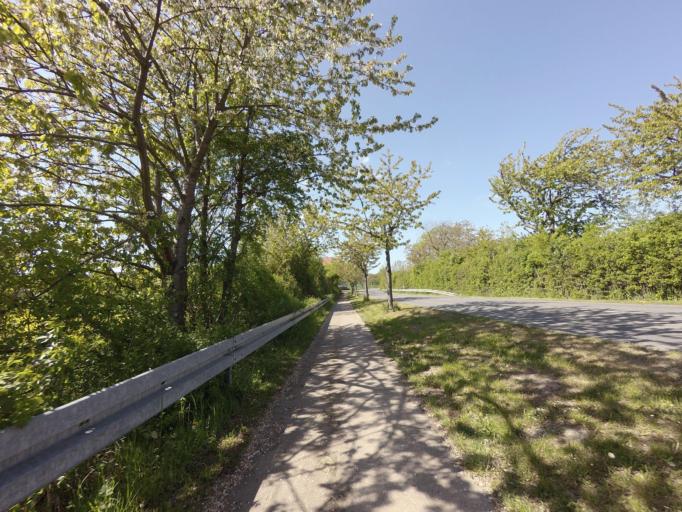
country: DE
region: Lower Saxony
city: Diekholzen
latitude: 52.1148
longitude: 9.9248
